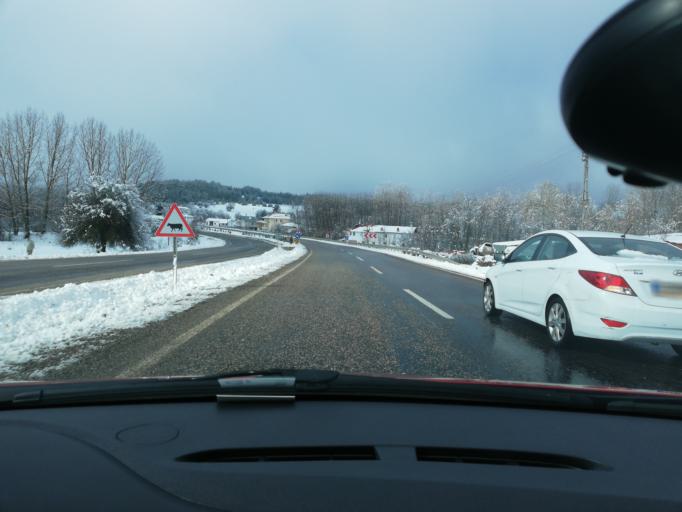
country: TR
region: Kastamonu
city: Ihsangazi
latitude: 41.3036
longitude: 33.5449
